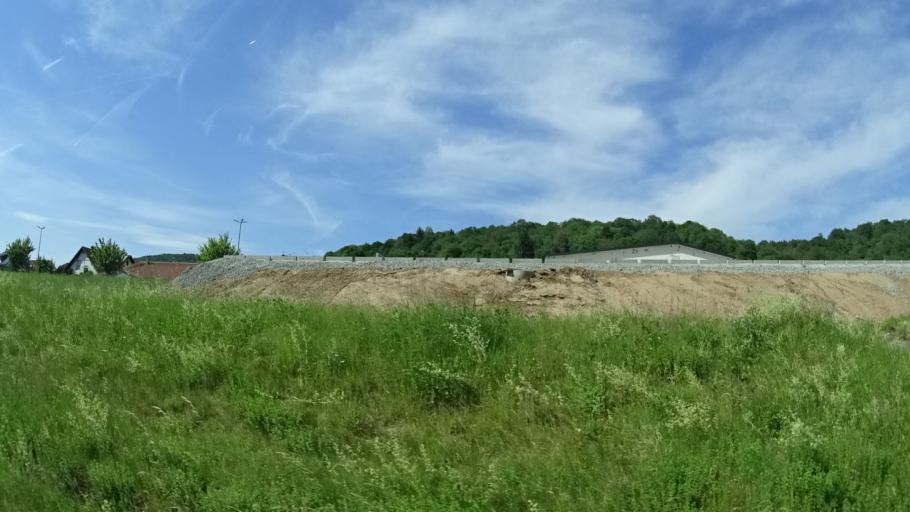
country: DE
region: Baden-Wuerttemberg
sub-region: Regierungsbezirk Stuttgart
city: Freudenberg
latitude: 49.7701
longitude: 9.3444
